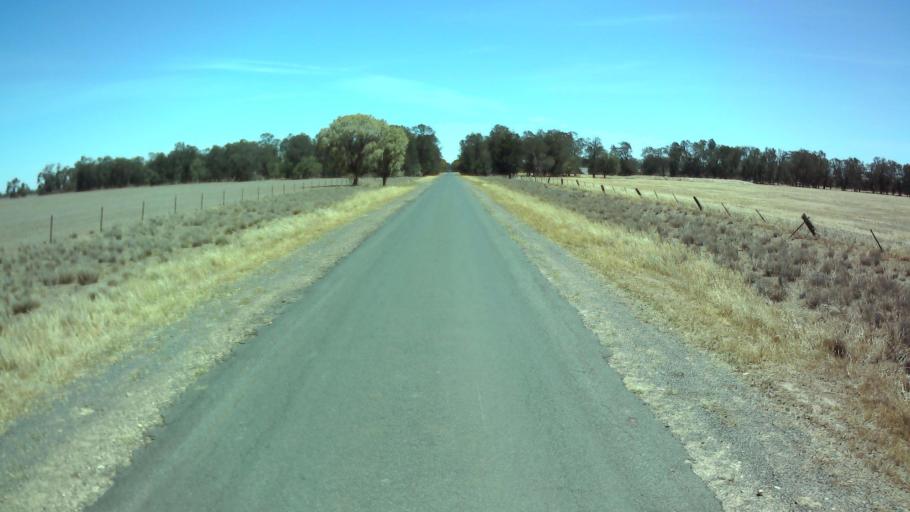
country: AU
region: New South Wales
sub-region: Weddin
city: Grenfell
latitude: -33.8655
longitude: 147.6929
